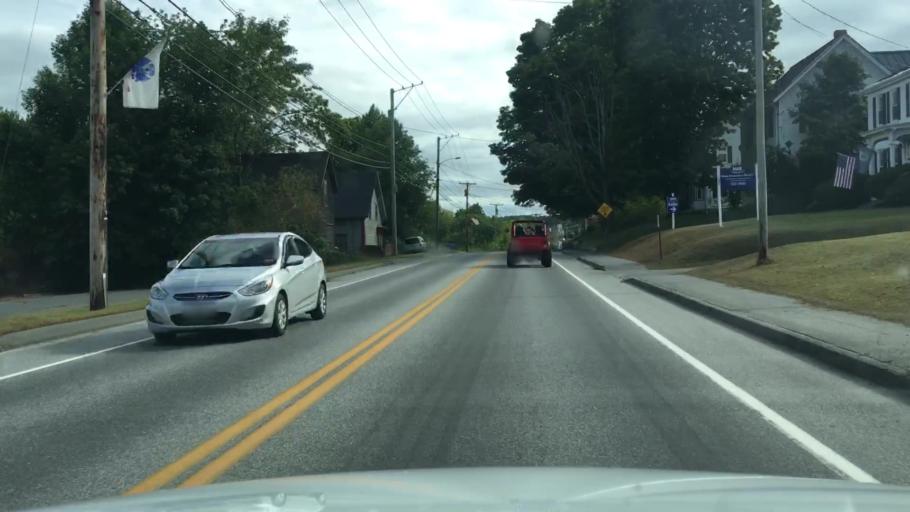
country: US
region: Maine
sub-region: Kennebec County
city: Farmingdale
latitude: 44.2407
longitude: -69.7711
